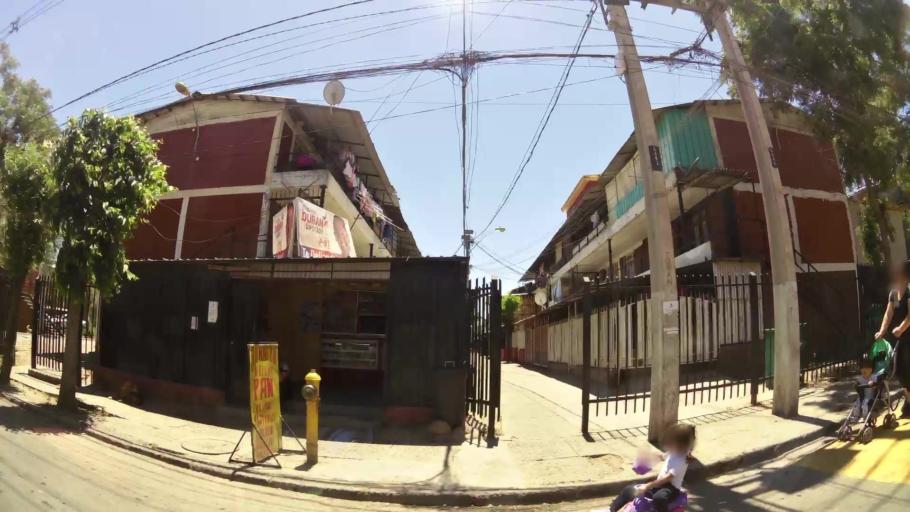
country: CL
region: Santiago Metropolitan
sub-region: Provincia de Santiago
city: La Pintana
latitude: -33.5782
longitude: -70.6667
